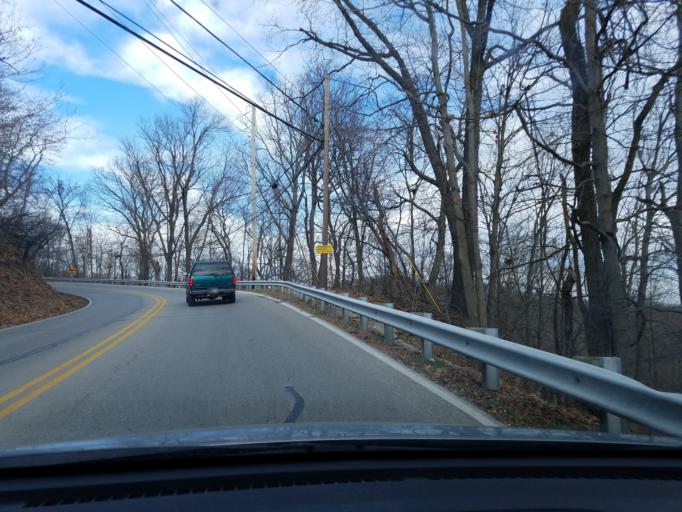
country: US
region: Indiana
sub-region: Floyd County
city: New Albany
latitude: 38.3207
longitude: -85.8569
